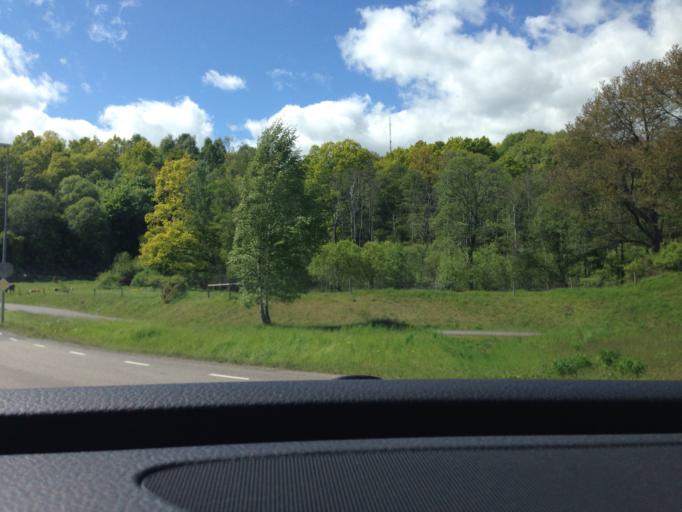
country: SE
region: Vaestra Goetaland
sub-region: Skovde Kommun
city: Skoevde
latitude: 58.4121
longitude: 13.8457
